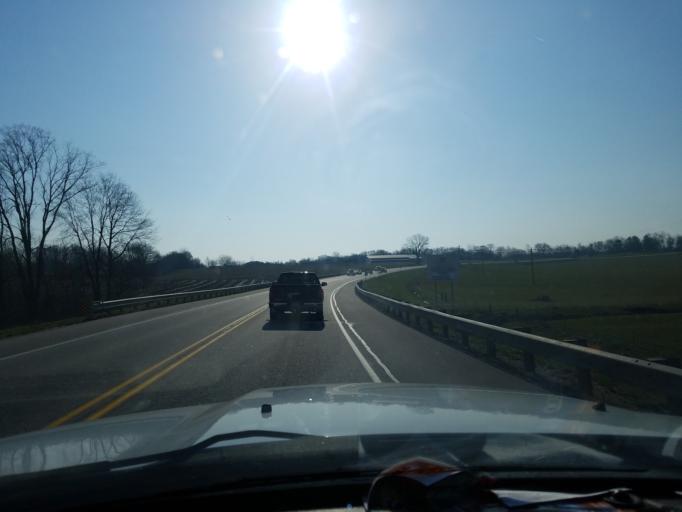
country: US
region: Indiana
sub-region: Monroe County
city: Ellettsville
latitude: 39.2814
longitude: -86.6836
